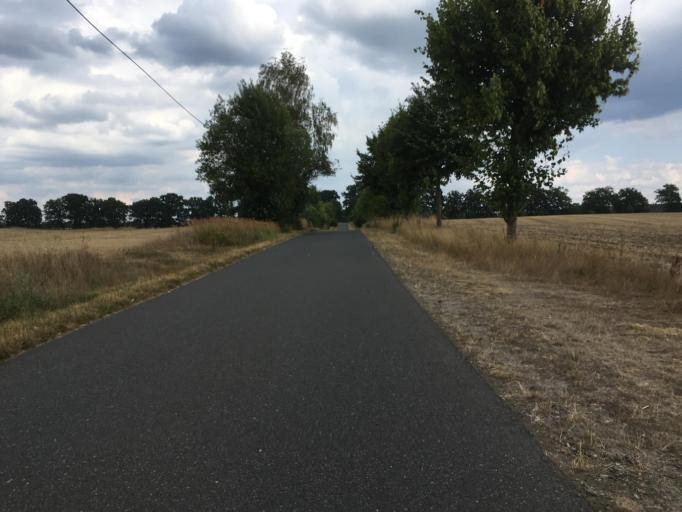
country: DE
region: Brandenburg
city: Lychen
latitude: 53.1166
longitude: 13.2612
